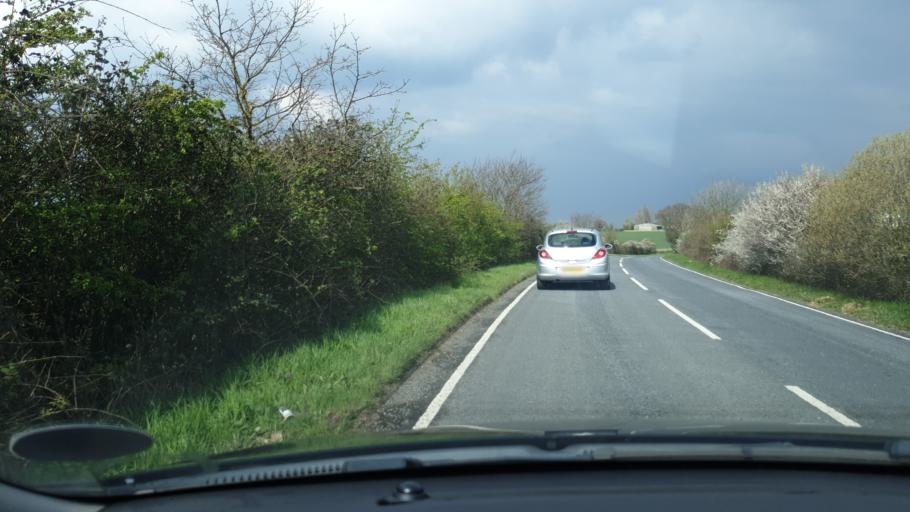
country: GB
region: England
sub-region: Essex
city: Mistley
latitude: 51.8964
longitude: 1.0930
